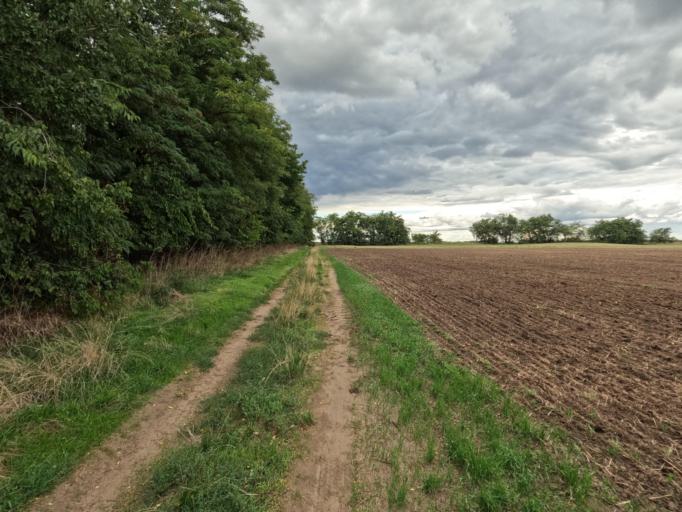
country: HU
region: Tolna
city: Tengelic
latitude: 46.5218
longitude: 18.6758
